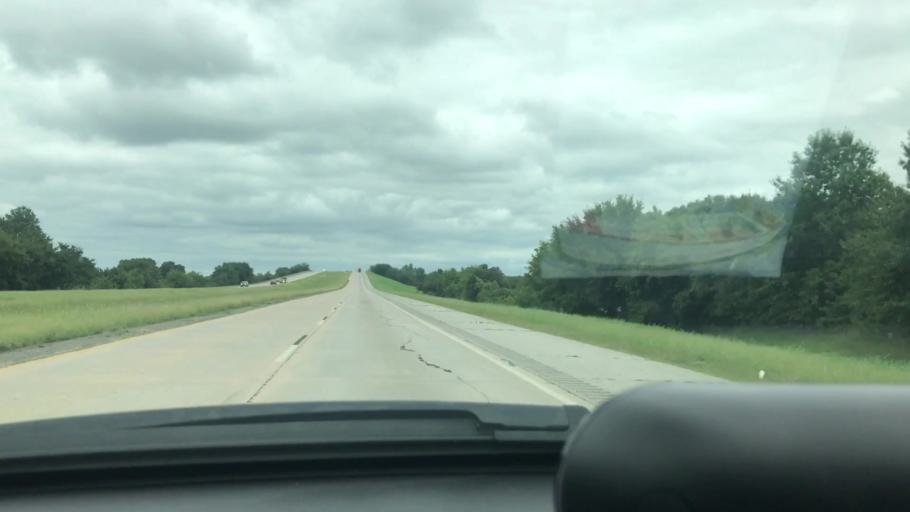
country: US
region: Oklahoma
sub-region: Wagoner County
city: Wagoner
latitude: 35.8777
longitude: -95.4026
